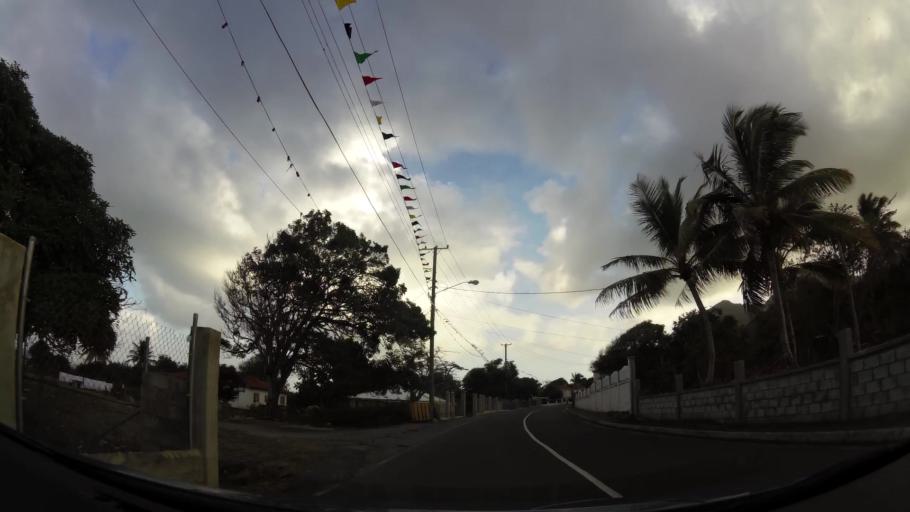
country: KN
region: Saint James Windwa
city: Newcastle
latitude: 17.1854
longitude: -62.5597
